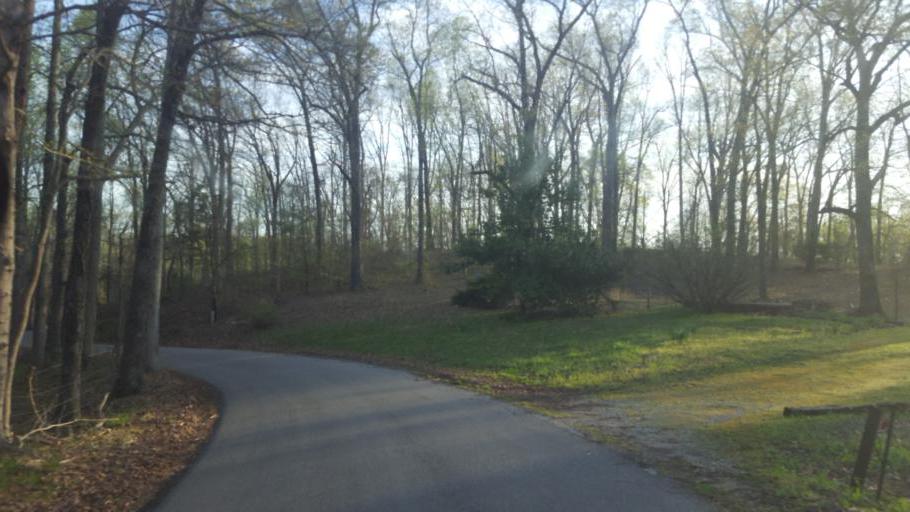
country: US
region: Kentucky
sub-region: Barren County
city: Cave City
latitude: 37.2182
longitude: -85.9983
